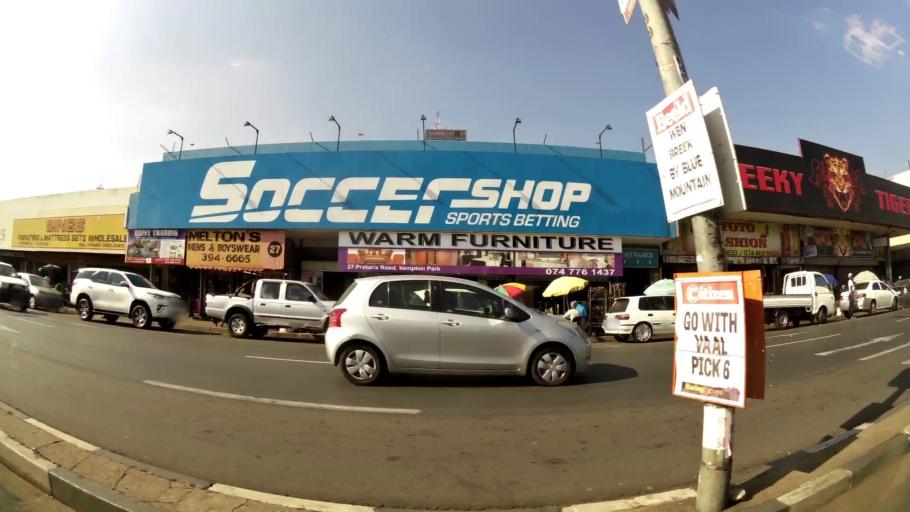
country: ZA
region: Gauteng
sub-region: City of Johannesburg Metropolitan Municipality
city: Modderfontein
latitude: -26.1058
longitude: 28.2274
